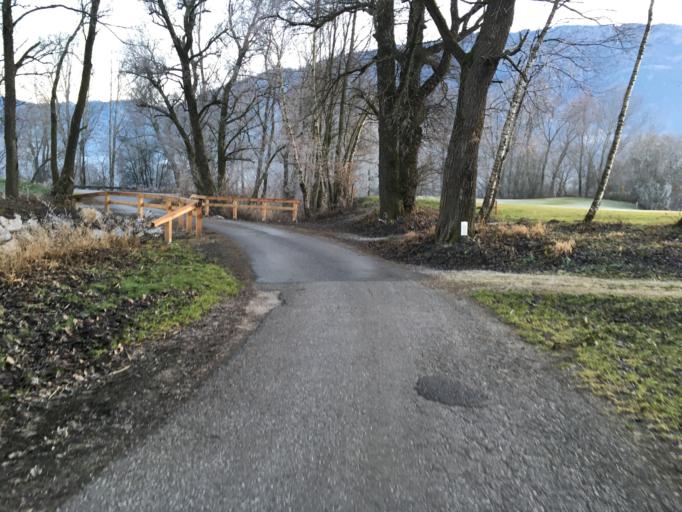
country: AT
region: Styria
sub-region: Politischer Bezirk Liezen
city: Weissenbach bei Liezen
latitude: 47.5555
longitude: 14.2025
